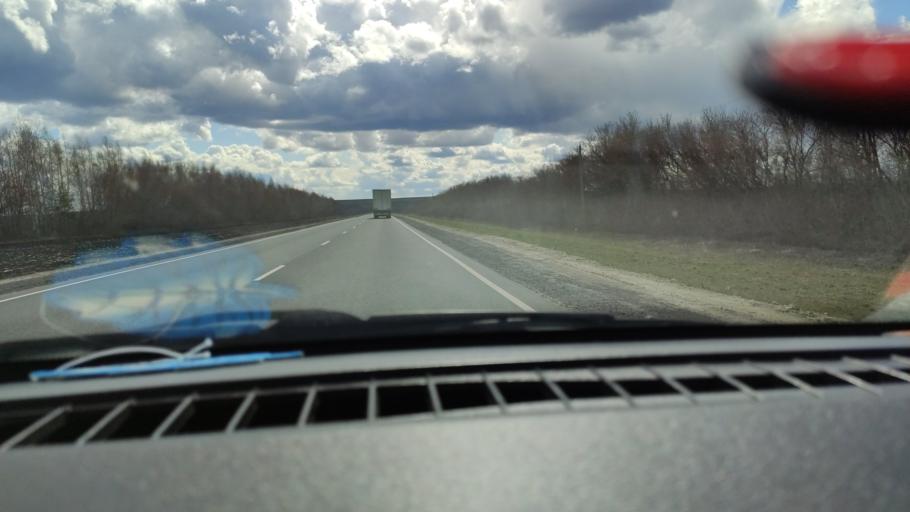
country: RU
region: Samara
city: Syzran'
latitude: 52.9809
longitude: 48.3130
